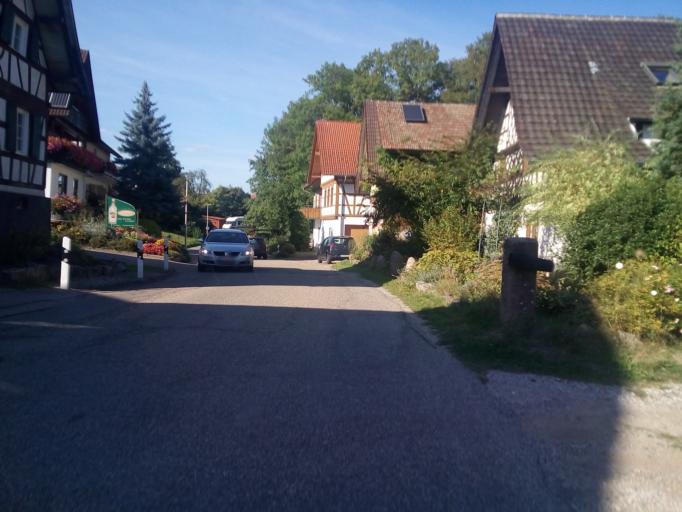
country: DE
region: Baden-Wuerttemberg
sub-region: Freiburg Region
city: Sasbach
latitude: 48.6268
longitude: 8.1051
